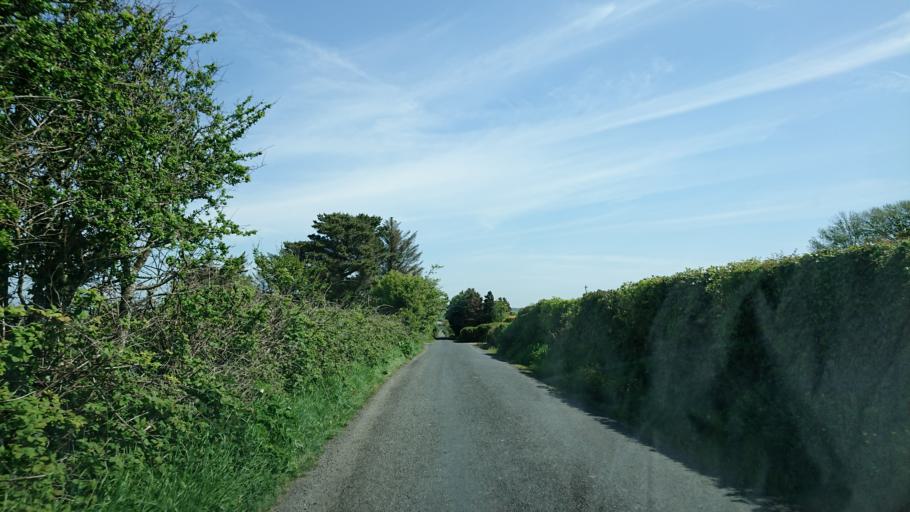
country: IE
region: Munster
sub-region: Waterford
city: Tra Mhor
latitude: 52.1526
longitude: -7.0744
